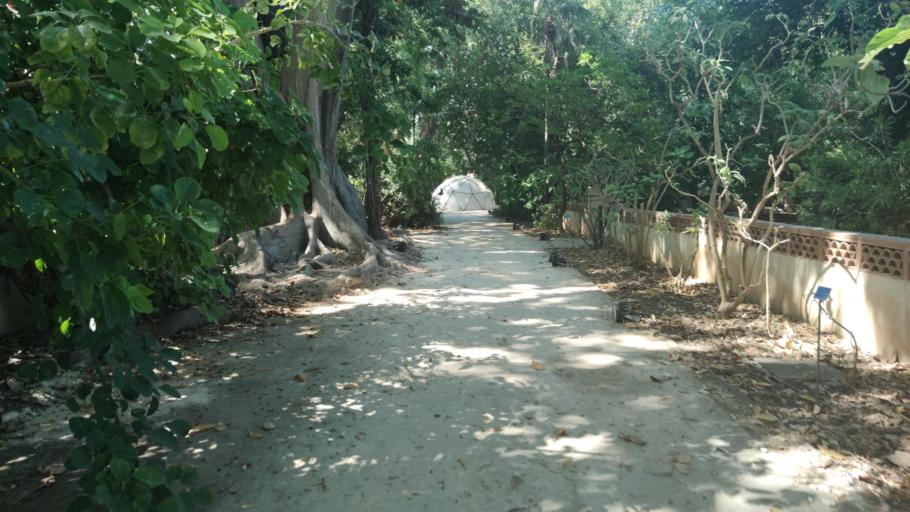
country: IT
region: Sicily
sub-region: Palermo
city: Palermo
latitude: 38.1123
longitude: 13.3741
